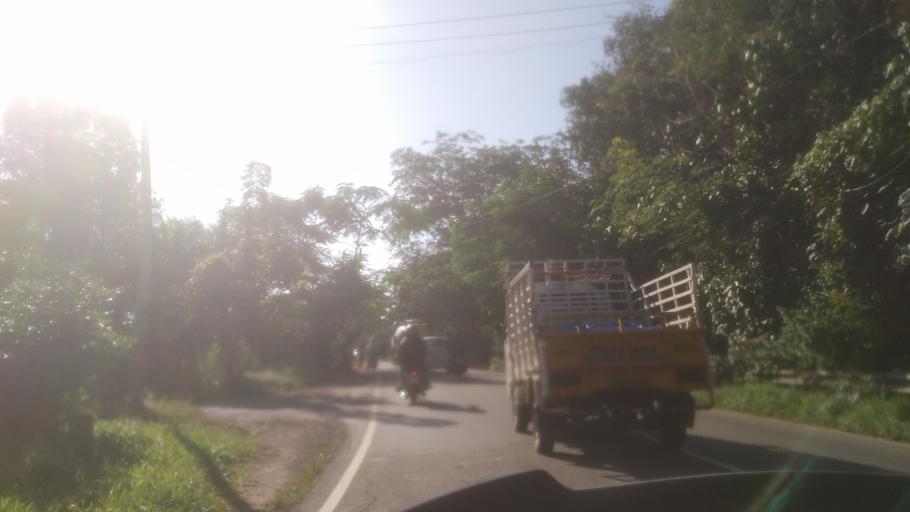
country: IN
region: Kerala
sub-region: Ernakulam
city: Ramamangalam
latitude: 9.9766
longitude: 76.5085
